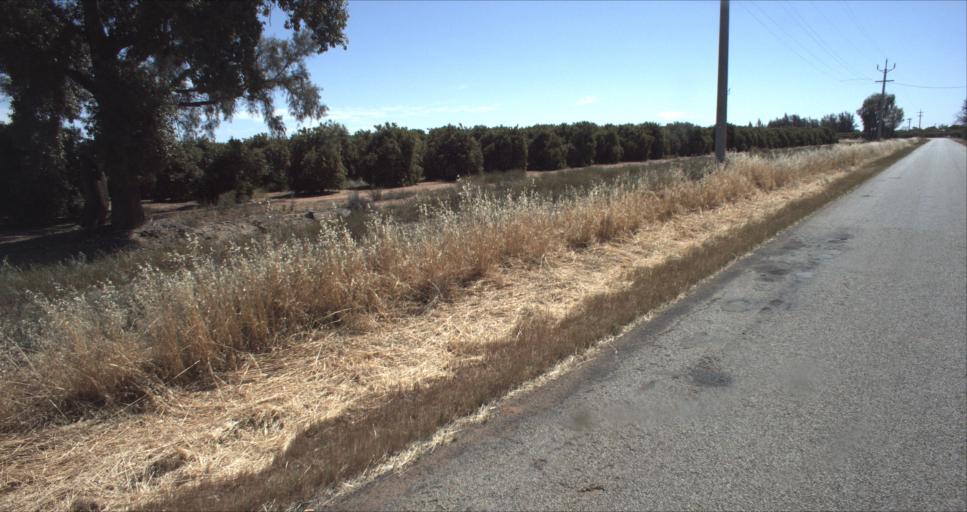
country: AU
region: New South Wales
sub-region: Leeton
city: Leeton
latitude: -34.5360
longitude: 146.3577
